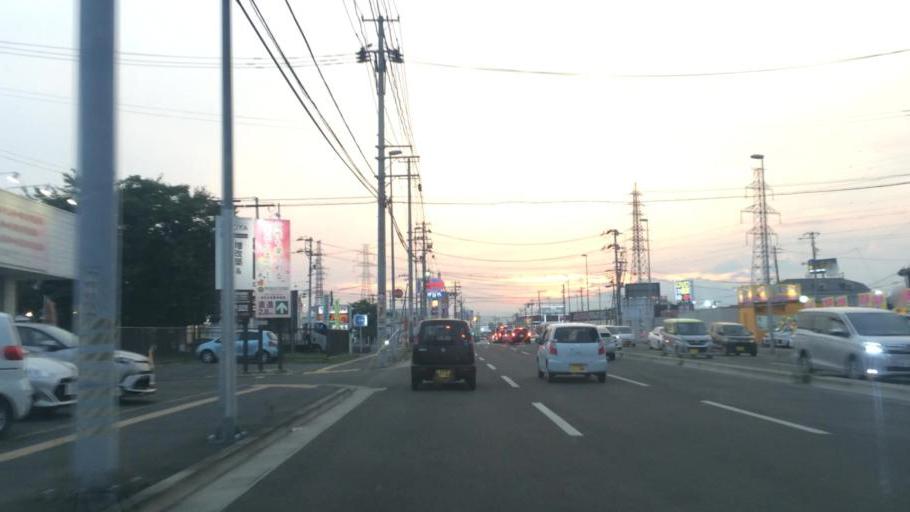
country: JP
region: Miyagi
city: Sendai-shi
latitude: 38.3150
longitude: 140.9022
